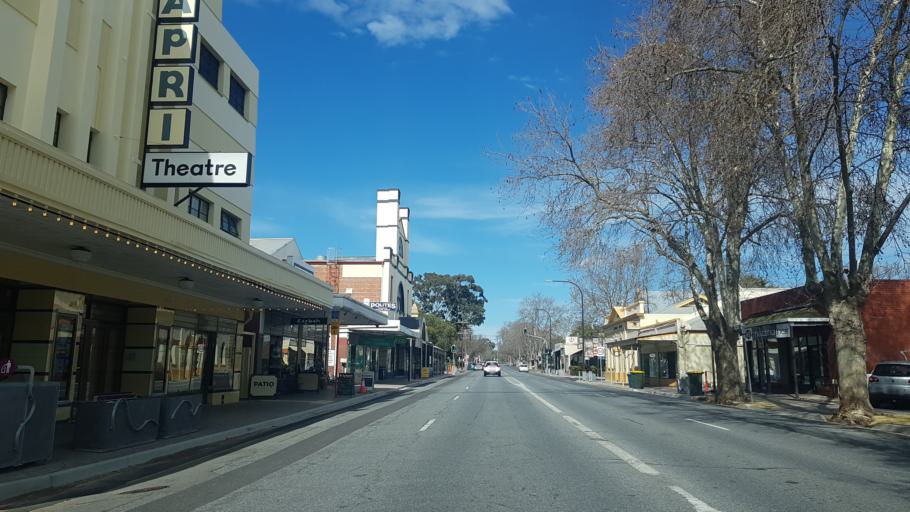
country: AU
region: South Australia
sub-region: Unley
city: Millswood
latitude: -34.9527
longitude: 138.5898
